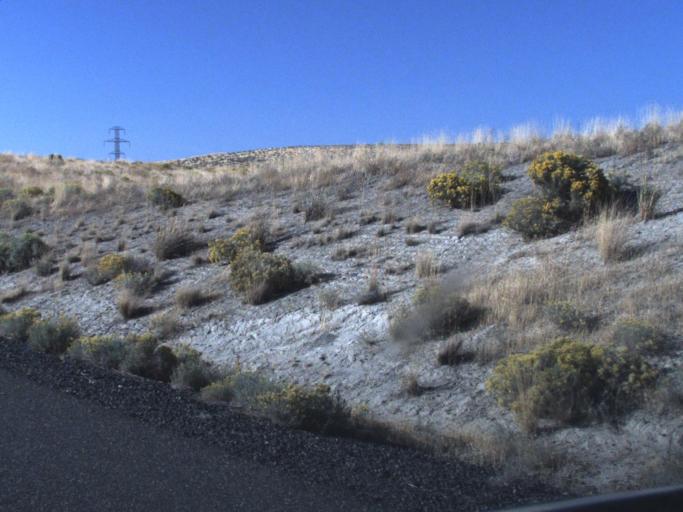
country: US
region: Washington
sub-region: Benton County
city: Highland
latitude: 46.1503
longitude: -119.1275
